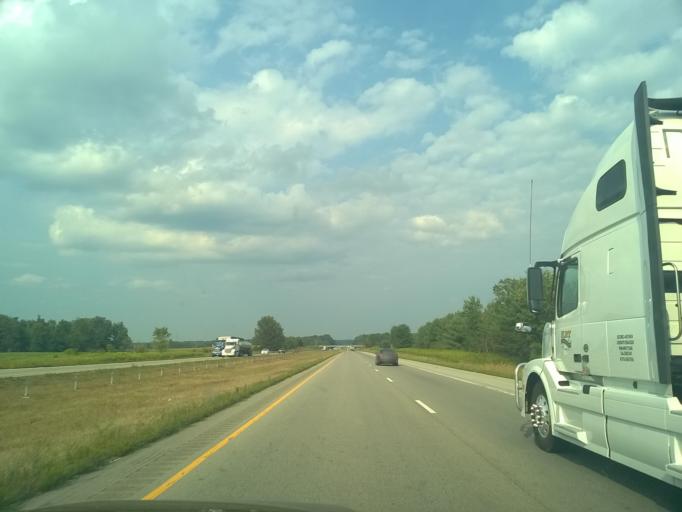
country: US
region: Indiana
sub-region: Clay County
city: Brazil
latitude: 39.4749
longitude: -87.0206
